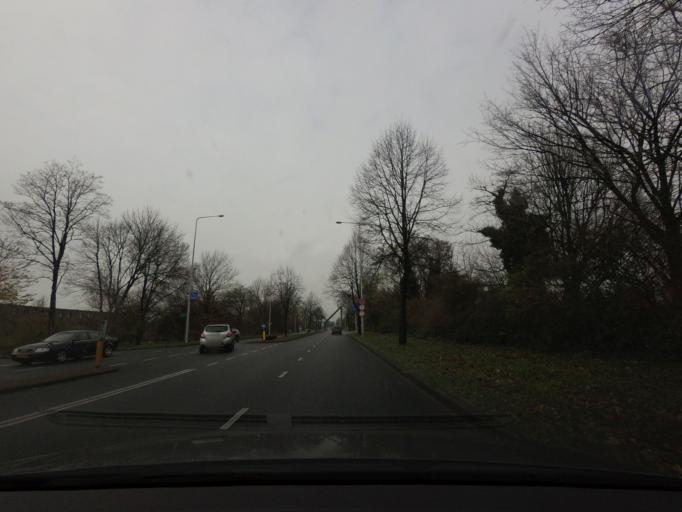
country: NL
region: North Holland
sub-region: Gemeente Amsterdam
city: Amsterdam-Zuidoost
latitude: 52.2986
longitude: 4.9684
